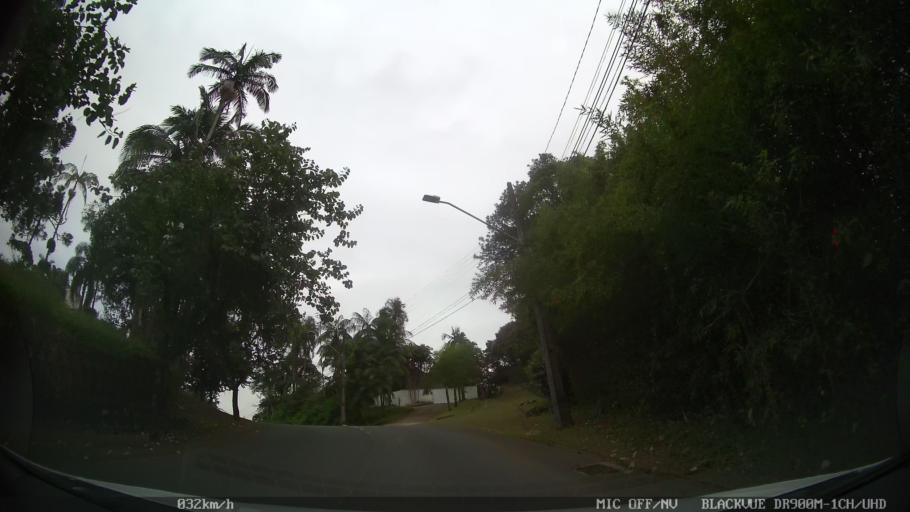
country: BR
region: Santa Catarina
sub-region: Joinville
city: Joinville
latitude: -26.2970
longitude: -48.8598
